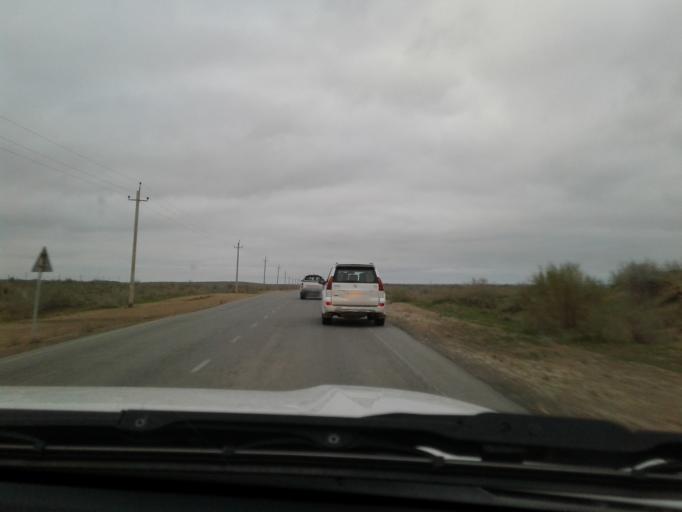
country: TM
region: Lebap
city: Farap
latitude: 39.0988
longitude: 63.7185
